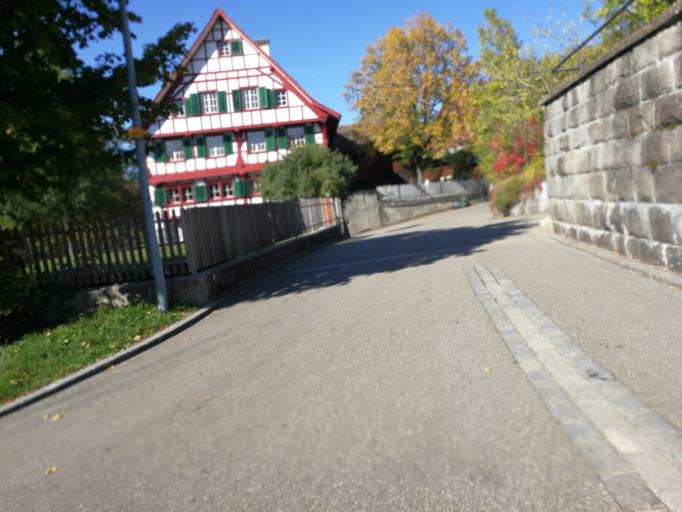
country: CH
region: Zurich
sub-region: Bezirk Uster
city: Aesch
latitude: 47.3378
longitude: 8.6723
